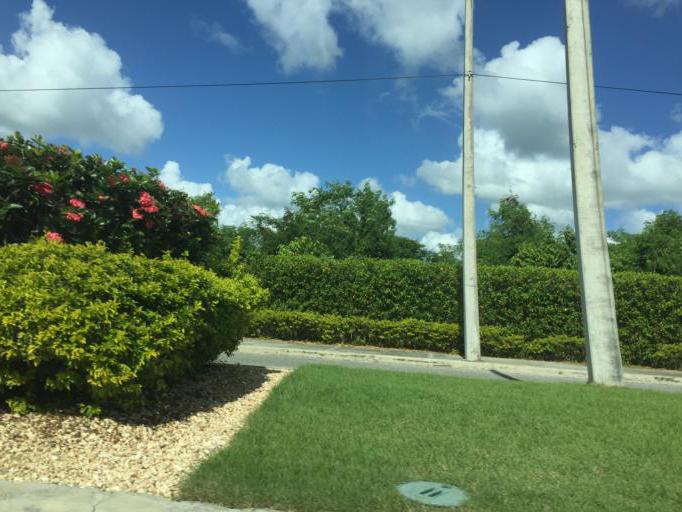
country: DO
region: Santo Domingo
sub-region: Santo Domingo
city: Boca Chica
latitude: 18.4605
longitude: -69.6581
